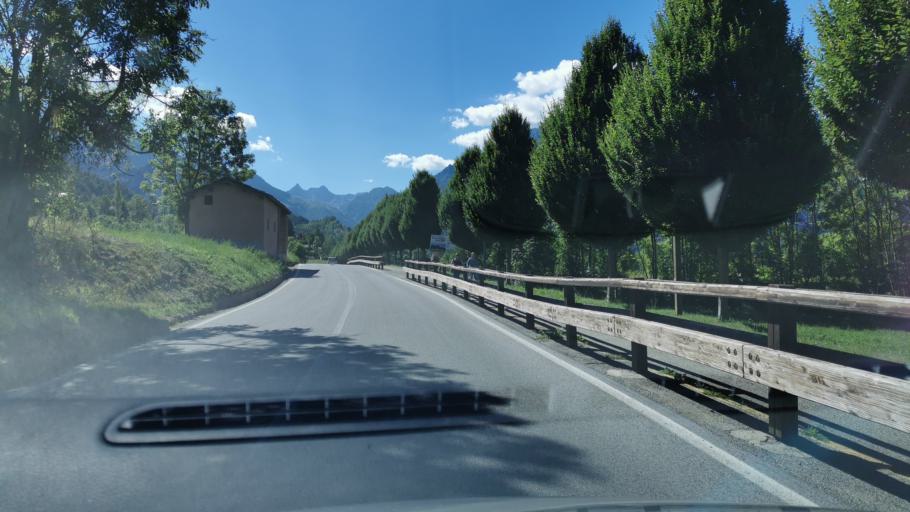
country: IT
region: Piedmont
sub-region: Provincia di Cuneo
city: Entracque
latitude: 44.2494
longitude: 7.3910
